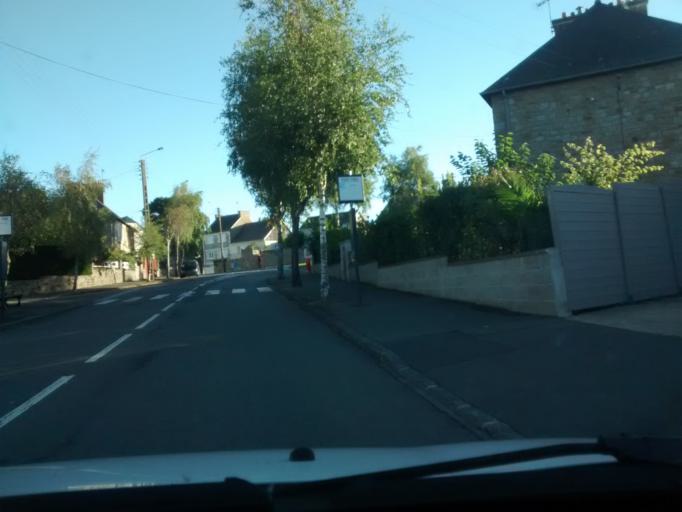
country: FR
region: Brittany
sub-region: Departement d'Ille-et-Vilaine
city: Saint-Malo
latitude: 48.6504
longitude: -1.9832
